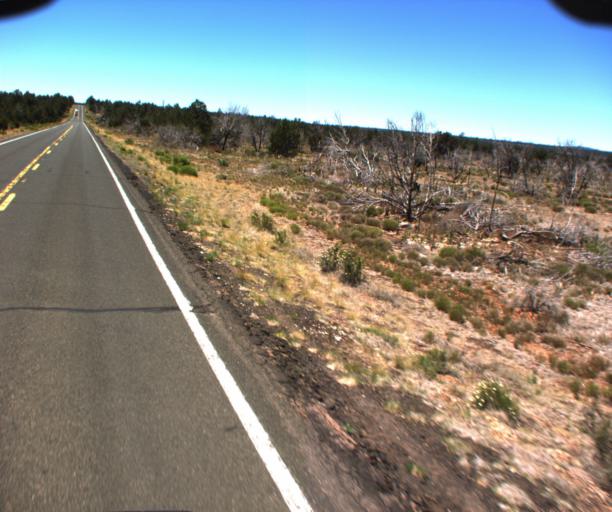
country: US
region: Arizona
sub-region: Coconino County
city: LeChee
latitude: 34.7106
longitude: -111.0953
